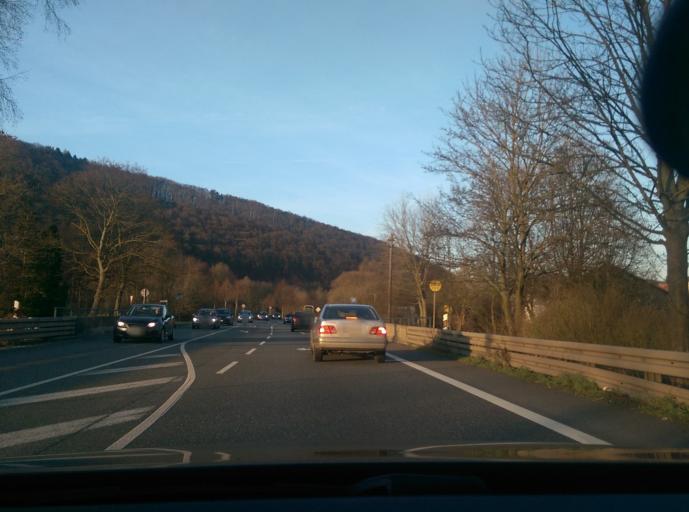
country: DE
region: Hesse
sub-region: Regierungsbezirk Kassel
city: Sontra
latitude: 51.1051
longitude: 9.9669
